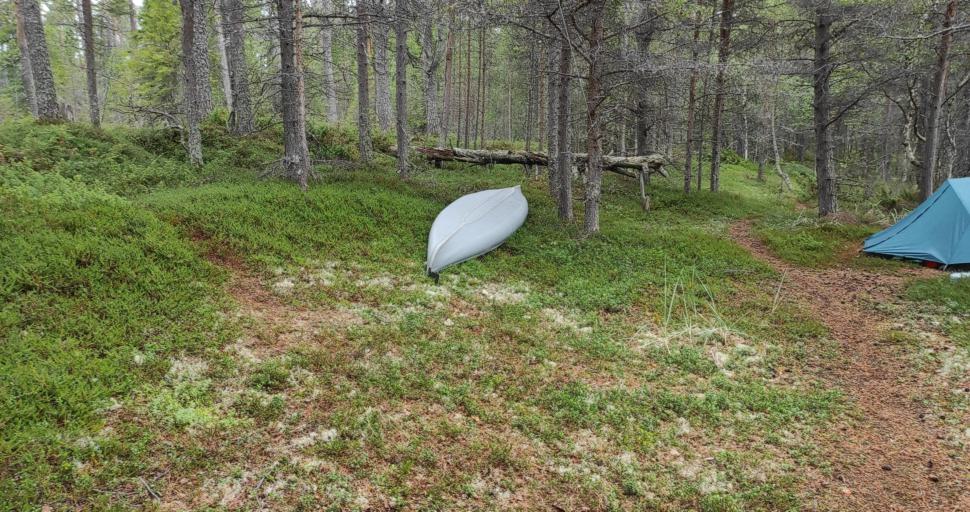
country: RU
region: Murmansk
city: Poyakonda
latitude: 66.7478
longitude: 32.9183
